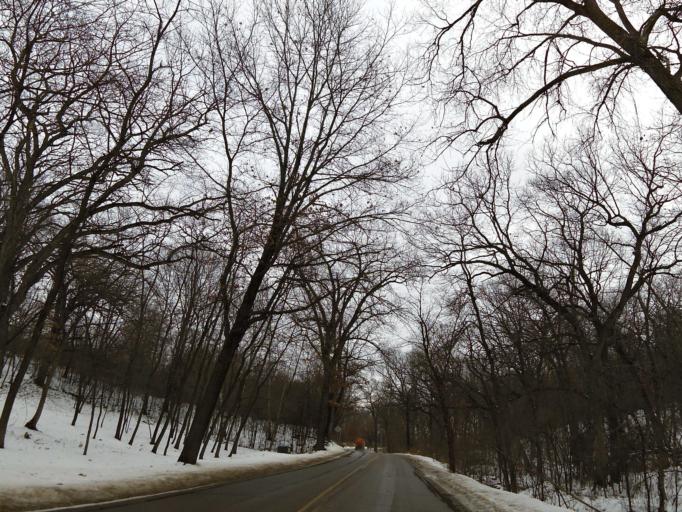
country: US
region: Minnesota
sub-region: Washington County
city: Bayport
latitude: 44.9953
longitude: -92.8003
